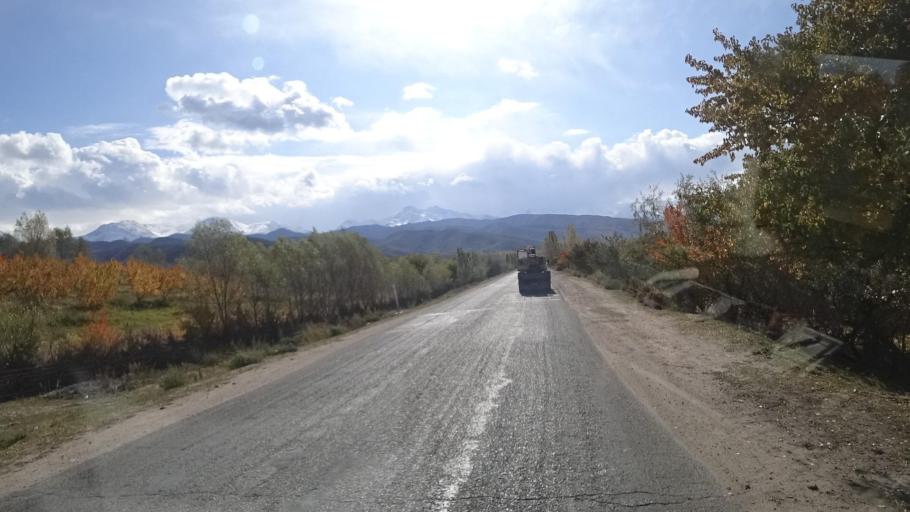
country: KG
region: Ysyk-Koel
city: Pokrovka
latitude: 42.2301
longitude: 77.7153
